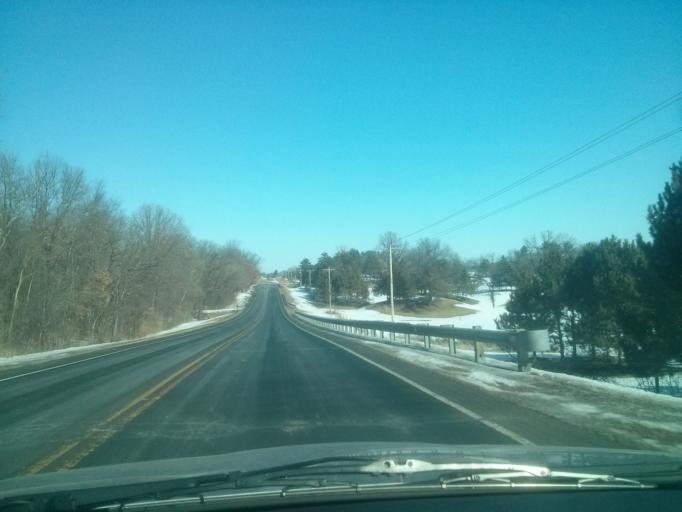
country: US
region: Wisconsin
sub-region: Saint Croix County
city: Somerset
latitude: 45.0842
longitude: -92.7362
